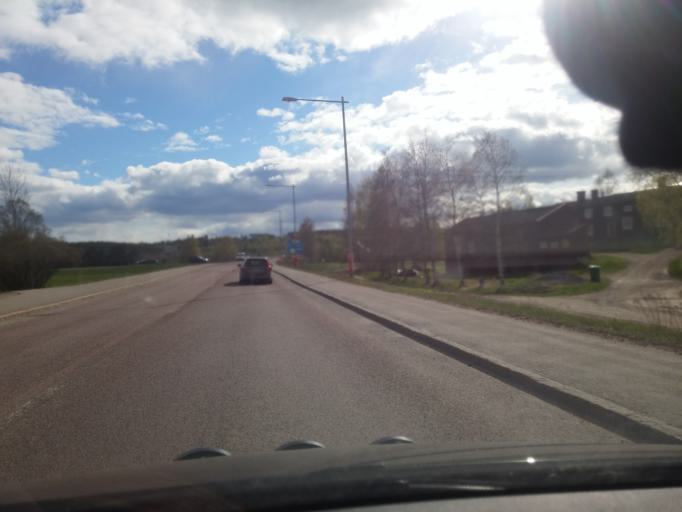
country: SE
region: Gaevleborg
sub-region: Ljusdals Kommun
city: Ljusdal
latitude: 61.8265
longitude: 16.0714
